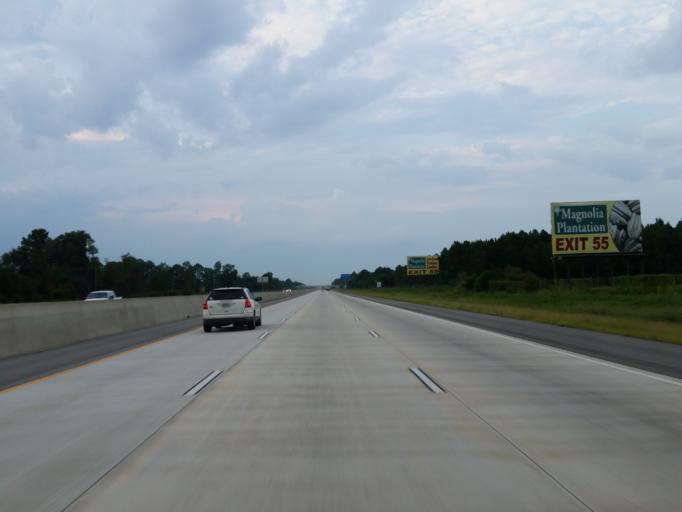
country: US
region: Georgia
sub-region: Cook County
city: Sparks
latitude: 31.2224
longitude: -83.4613
